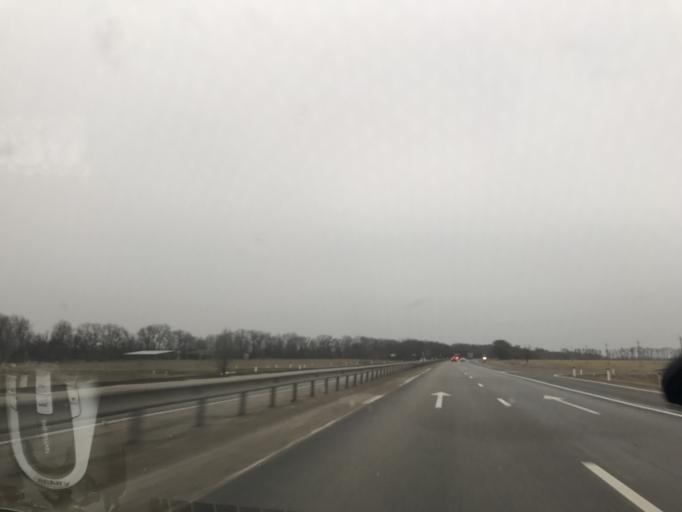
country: RU
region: Krasnodarskiy
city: Pavlovskaya
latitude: 46.1821
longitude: 39.8340
